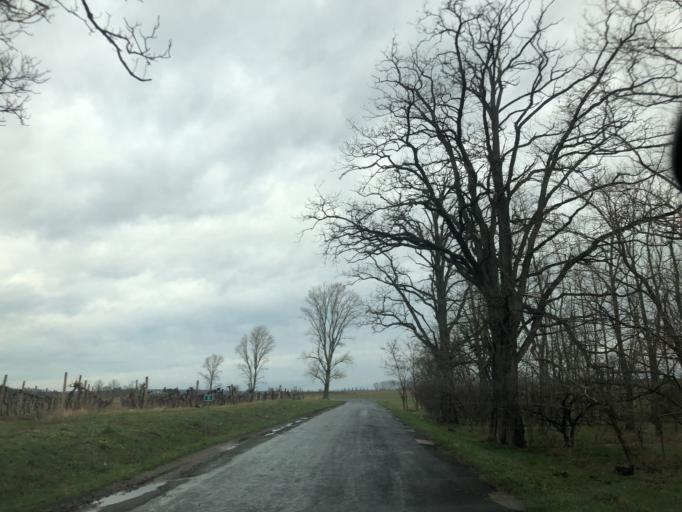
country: HU
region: Gyor-Moson-Sopron
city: Fertorakos
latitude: 47.6998
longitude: 16.6598
